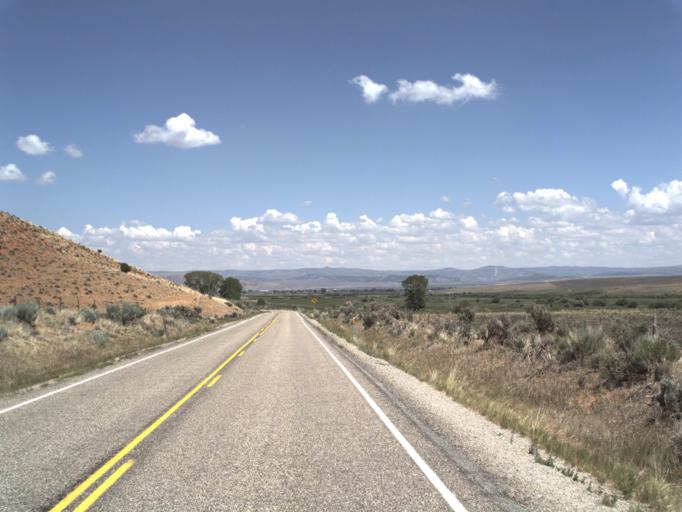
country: US
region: Utah
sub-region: Rich County
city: Randolph
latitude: 41.5090
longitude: -111.2323
